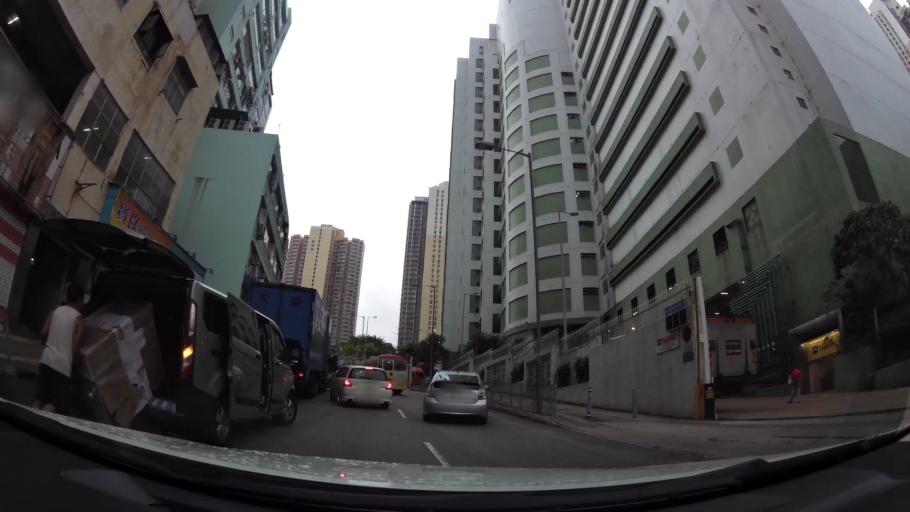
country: HK
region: Tsuen Wan
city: Tsuen Wan
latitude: 22.3699
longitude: 114.1294
